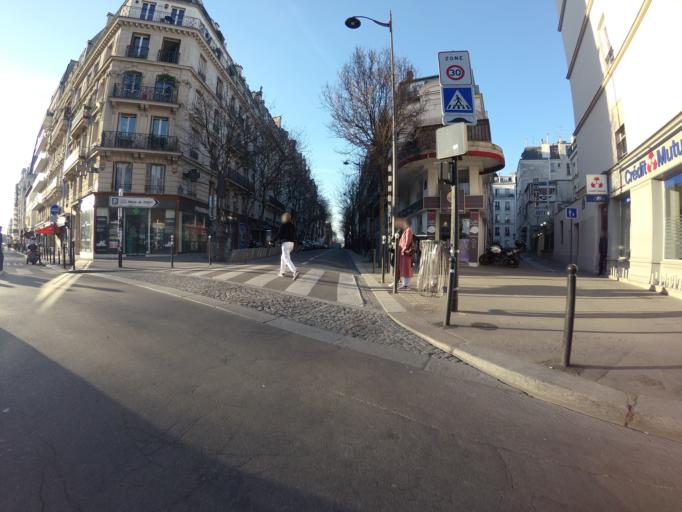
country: FR
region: Ile-de-France
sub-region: Paris
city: Saint-Ouen
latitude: 48.8825
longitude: 2.3247
